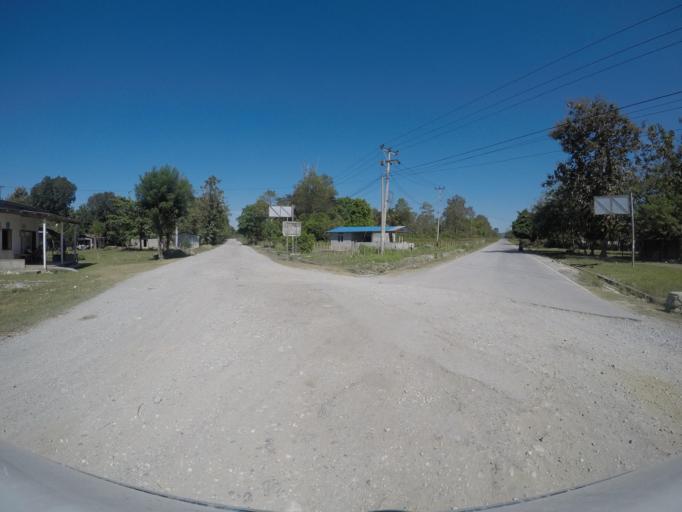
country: TL
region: Viqueque
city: Viqueque
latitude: -8.9770
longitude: 126.0425
